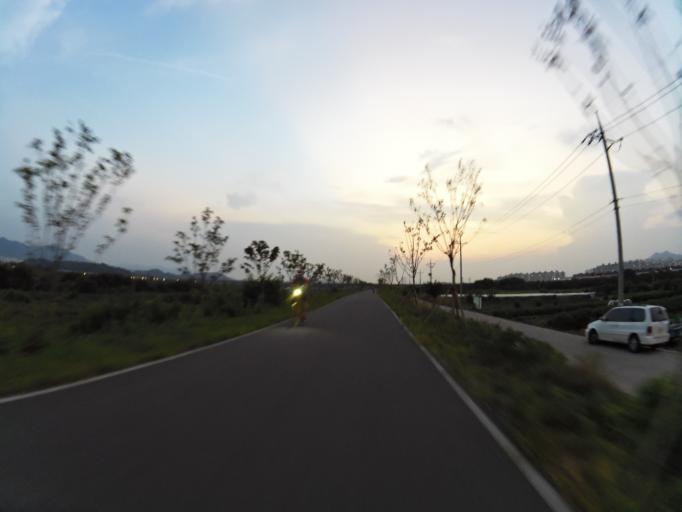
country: KR
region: Gyeongsangbuk-do
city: Gyeongsan-si
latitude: 35.8582
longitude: 128.7324
